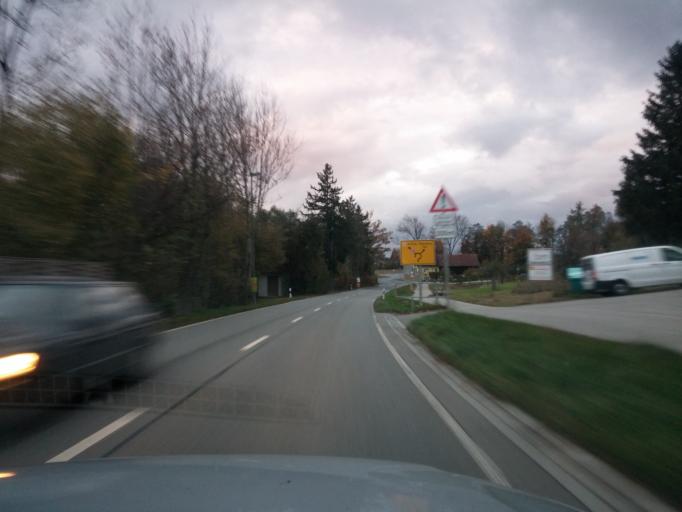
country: DE
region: Bavaria
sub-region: Upper Bavaria
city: Grafing bei Munchen
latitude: 48.0383
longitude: 11.9783
